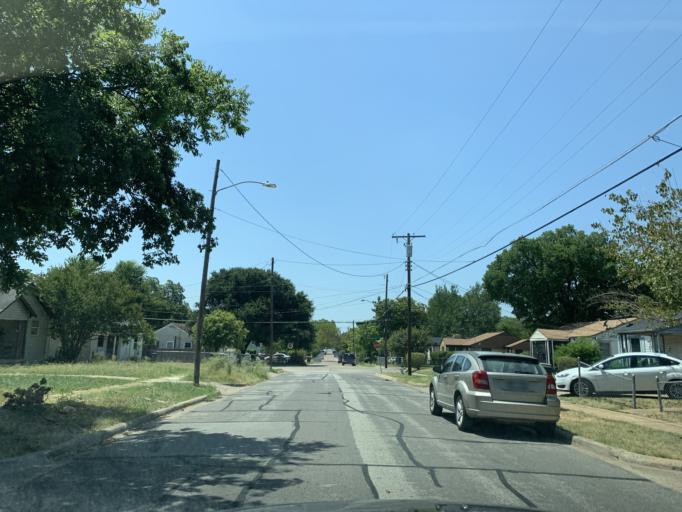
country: US
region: Texas
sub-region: Dallas County
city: Dallas
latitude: 32.6916
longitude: -96.8006
